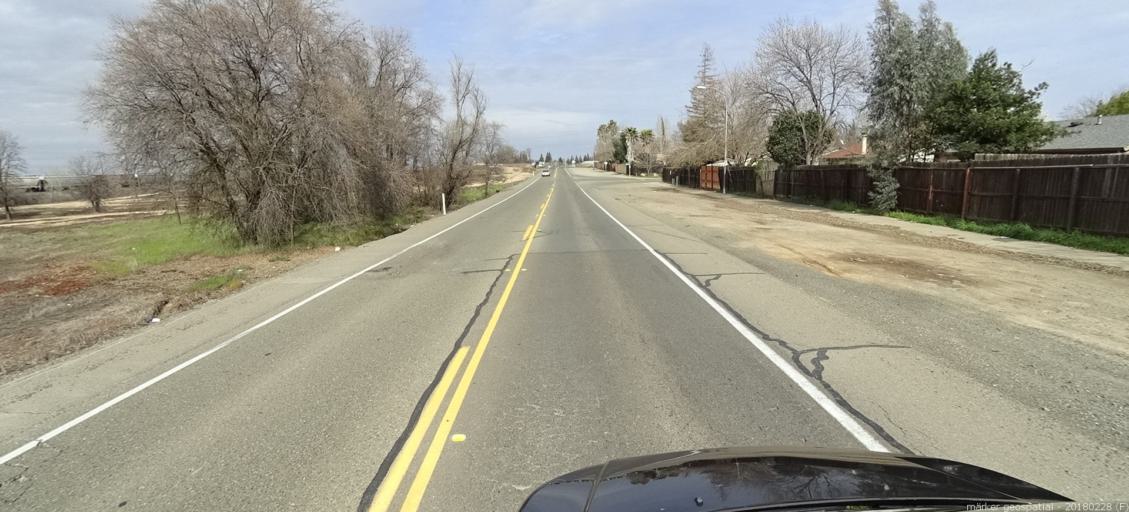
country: US
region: California
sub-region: Sacramento County
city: Antelope
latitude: 38.7210
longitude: -121.3109
